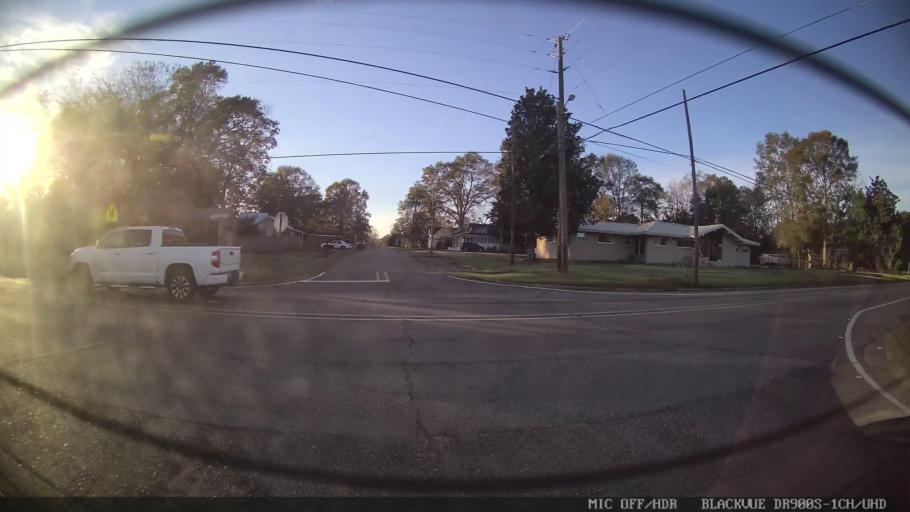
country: US
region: Mississippi
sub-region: Lamar County
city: Lumberton
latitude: 30.9992
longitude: -89.4531
